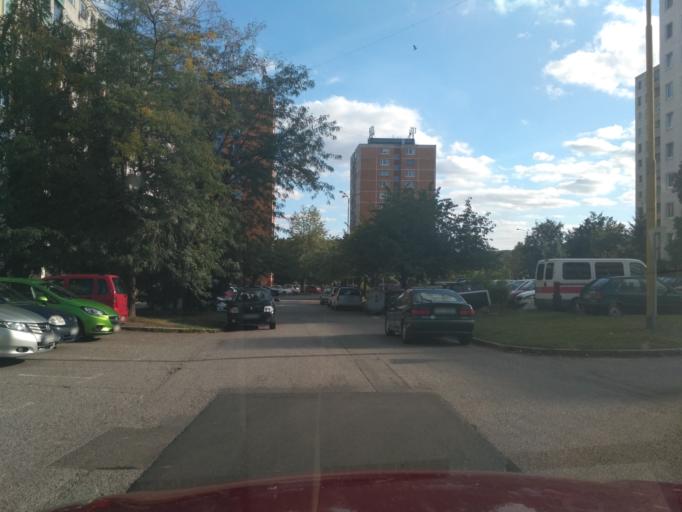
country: SK
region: Kosicky
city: Kosice
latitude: 48.7095
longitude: 21.2134
